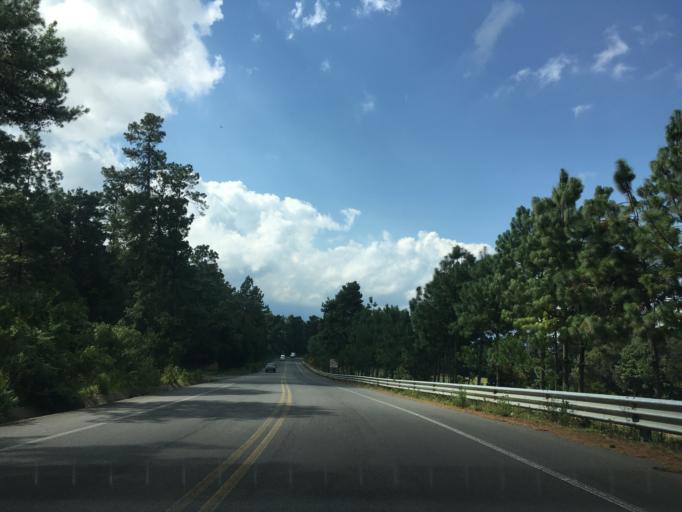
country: MX
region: Michoacan
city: Angahuan
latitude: 19.5710
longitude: -102.2742
